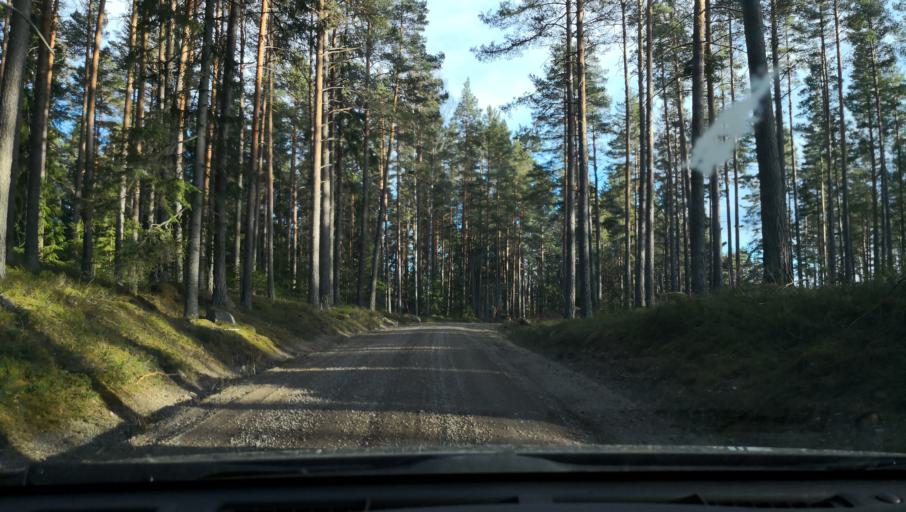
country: SE
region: Vaestmanland
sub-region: Arboga Kommun
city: Arboga
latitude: 59.4349
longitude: 15.7524
